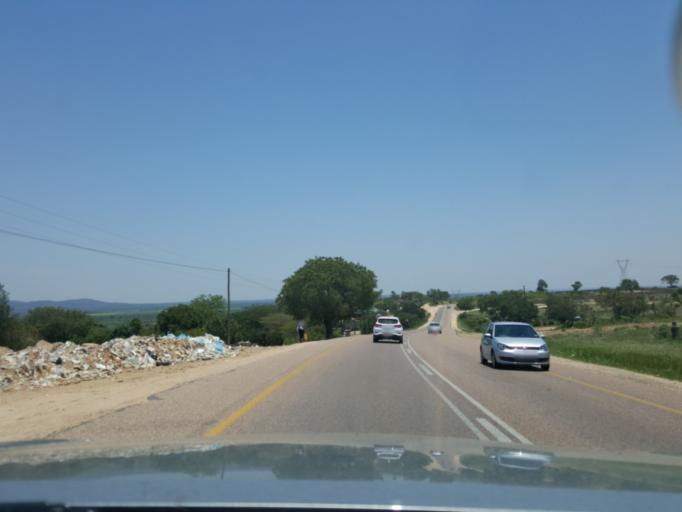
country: ZA
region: Limpopo
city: Thulamahashi
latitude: -24.5906
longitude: 31.0405
